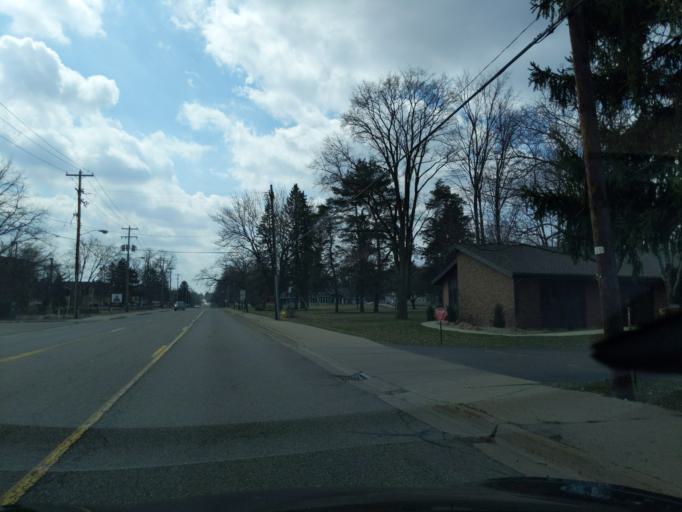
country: US
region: Michigan
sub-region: Calhoun County
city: Lakeview
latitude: 42.2583
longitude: -85.1987
